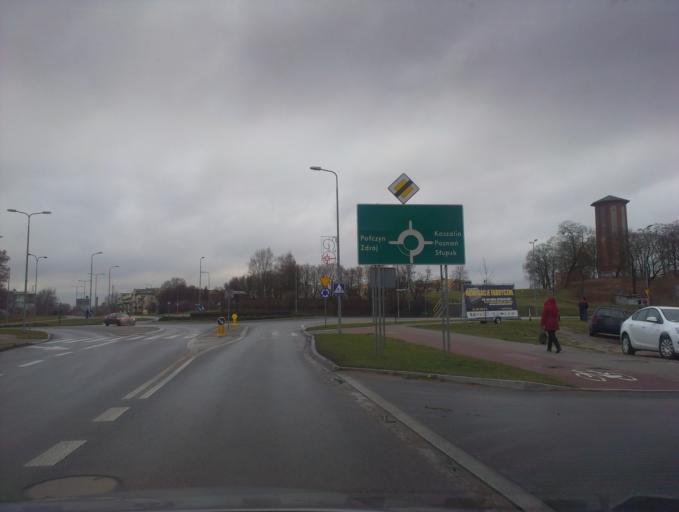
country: PL
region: West Pomeranian Voivodeship
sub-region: Powiat szczecinecki
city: Szczecinek
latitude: 53.7100
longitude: 16.6980
